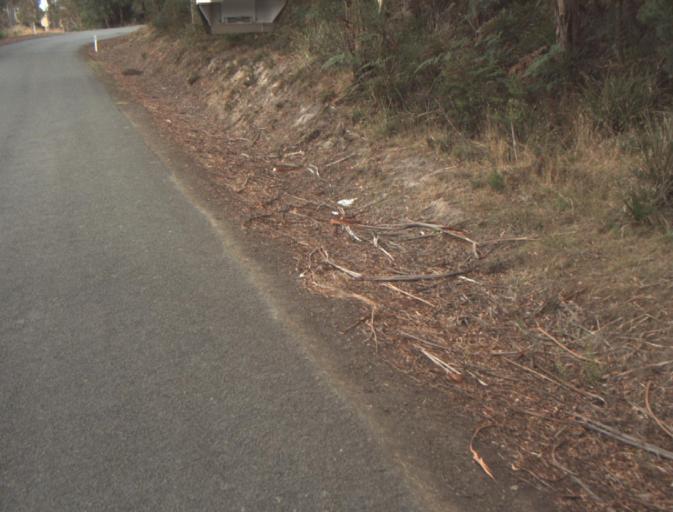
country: AU
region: Tasmania
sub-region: Launceston
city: Mayfield
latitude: -41.2390
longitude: 147.1967
